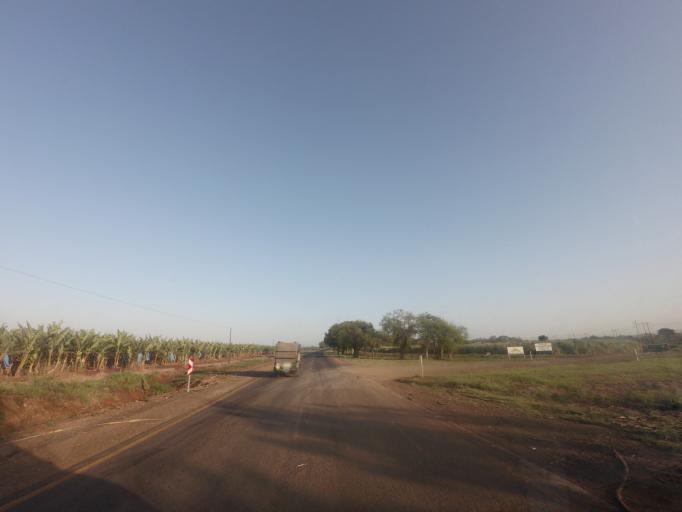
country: ZA
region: Mpumalanga
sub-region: Ehlanzeni District
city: Komatipoort
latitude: -25.3891
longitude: 31.9132
